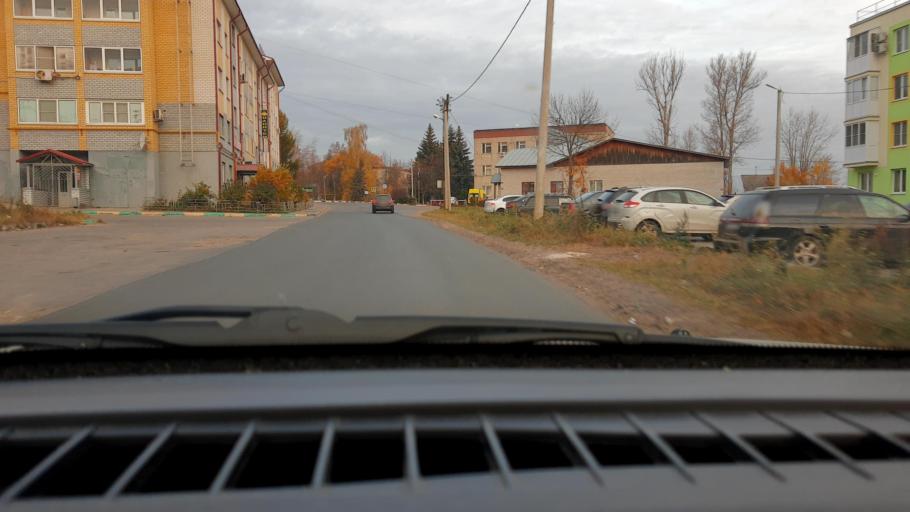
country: RU
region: Nizjnij Novgorod
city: Burevestnik
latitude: 56.2042
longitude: 43.8819
